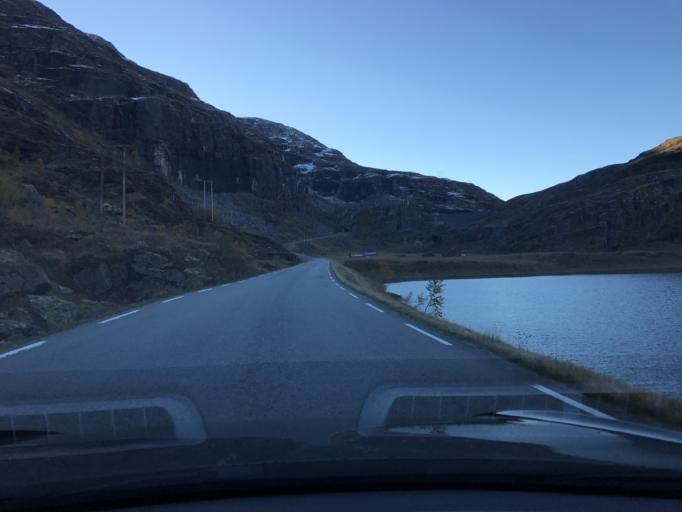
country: NO
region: Sogn og Fjordane
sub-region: Laerdal
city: Laerdalsoyri
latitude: 60.8053
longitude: 7.5632
